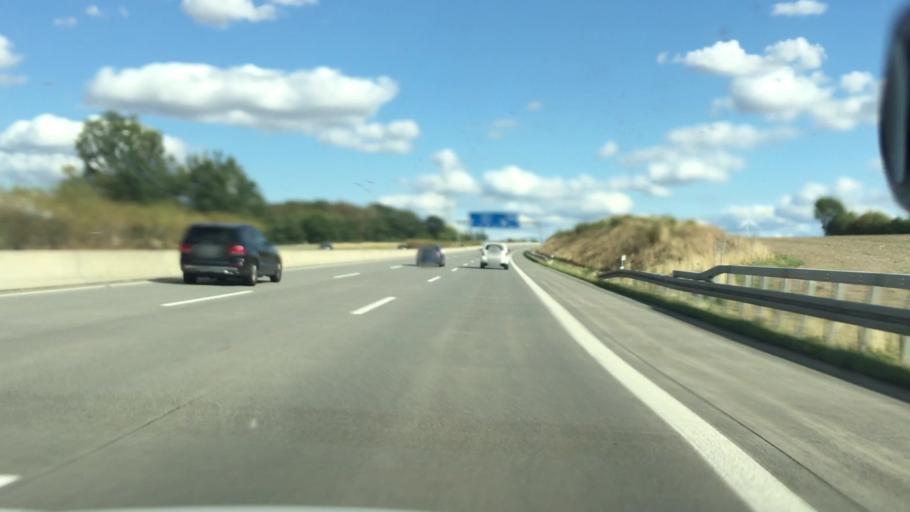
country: DE
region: Thuringia
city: Thonhausen
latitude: 50.8536
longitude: 12.3260
